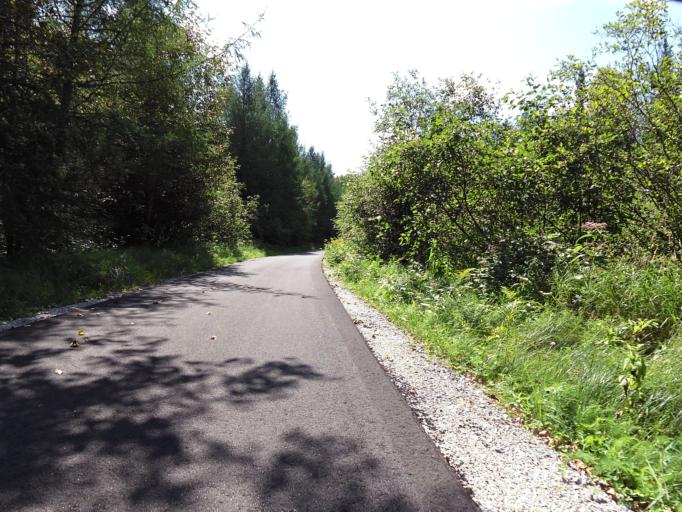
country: CA
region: Quebec
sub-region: Outaouais
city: Maniwaki
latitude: 46.1716
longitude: -76.0402
